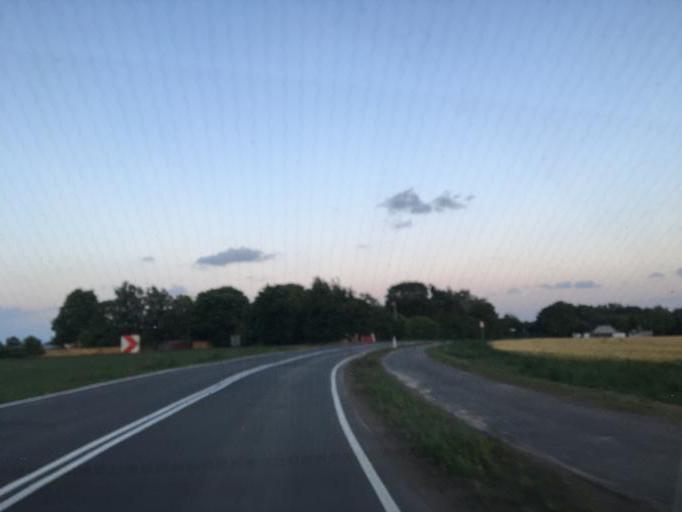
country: DK
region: Zealand
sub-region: Solrod Kommune
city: Havdrup
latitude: 55.5183
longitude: 12.1420
